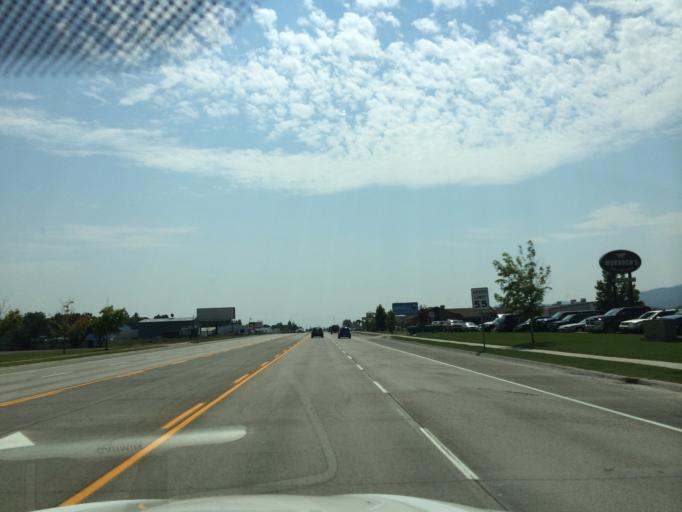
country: US
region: Montana
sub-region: Flathead County
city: Kalispell
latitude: 48.1750
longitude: -114.2981
